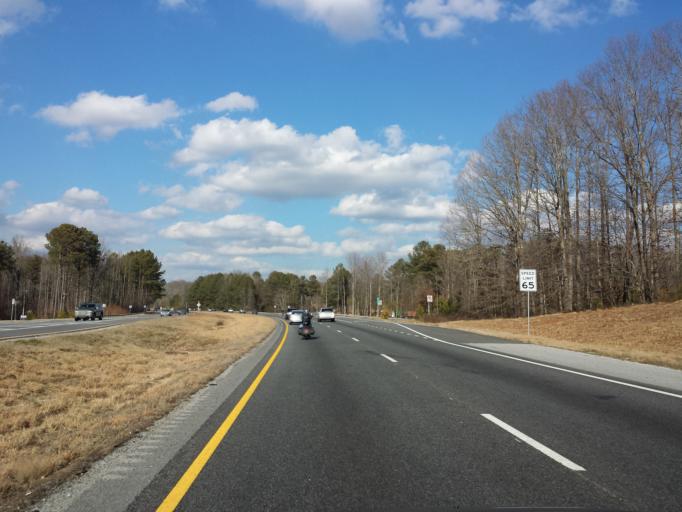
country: US
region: Georgia
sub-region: Forsyth County
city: Cumming
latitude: 34.2721
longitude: -84.0785
